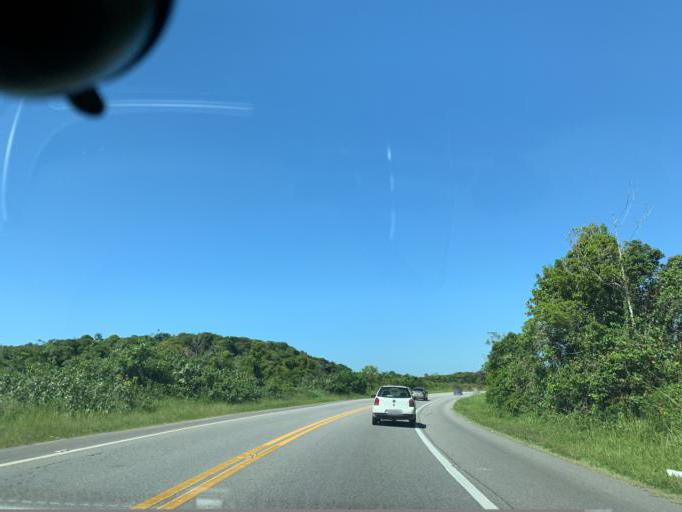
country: BR
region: Sao Paulo
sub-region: Bertioga
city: Bertioga
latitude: -23.7770
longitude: -45.9651
